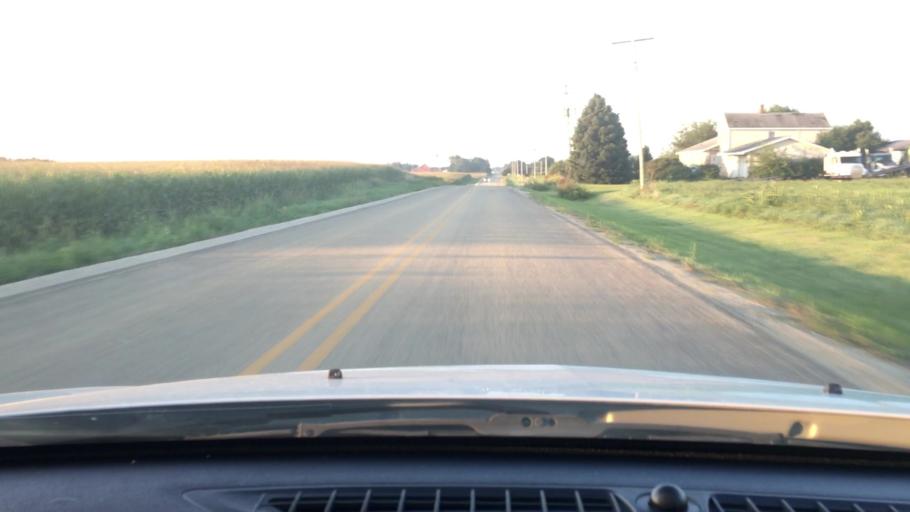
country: US
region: Illinois
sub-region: DeKalb County
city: Waterman
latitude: 41.8096
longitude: -88.7734
